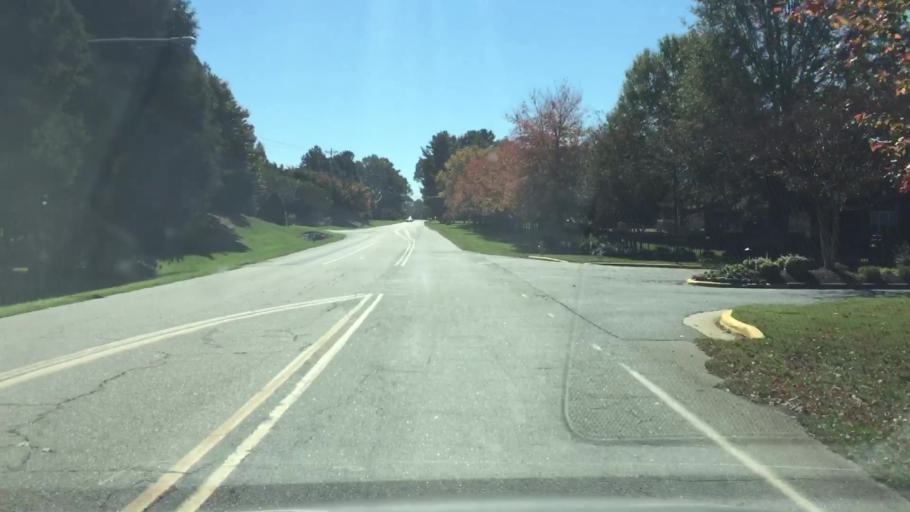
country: US
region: North Carolina
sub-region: Iredell County
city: Mooresville
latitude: 35.5462
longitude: -80.7897
